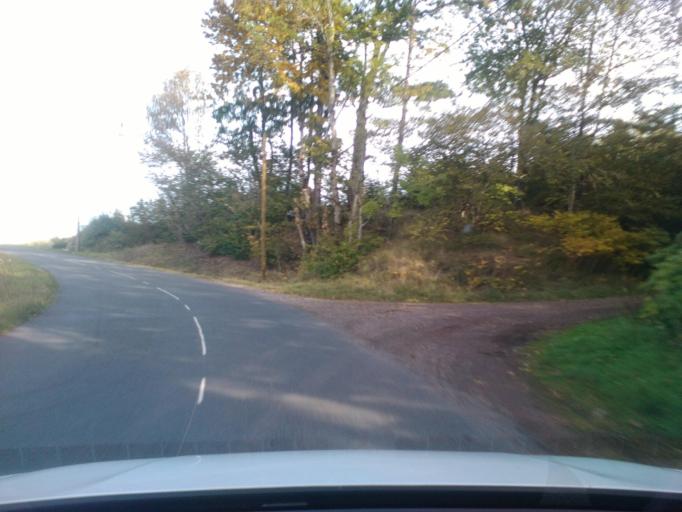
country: FR
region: Lorraine
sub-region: Departement des Vosges
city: Senones
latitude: 48.3563
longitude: 7.0257
